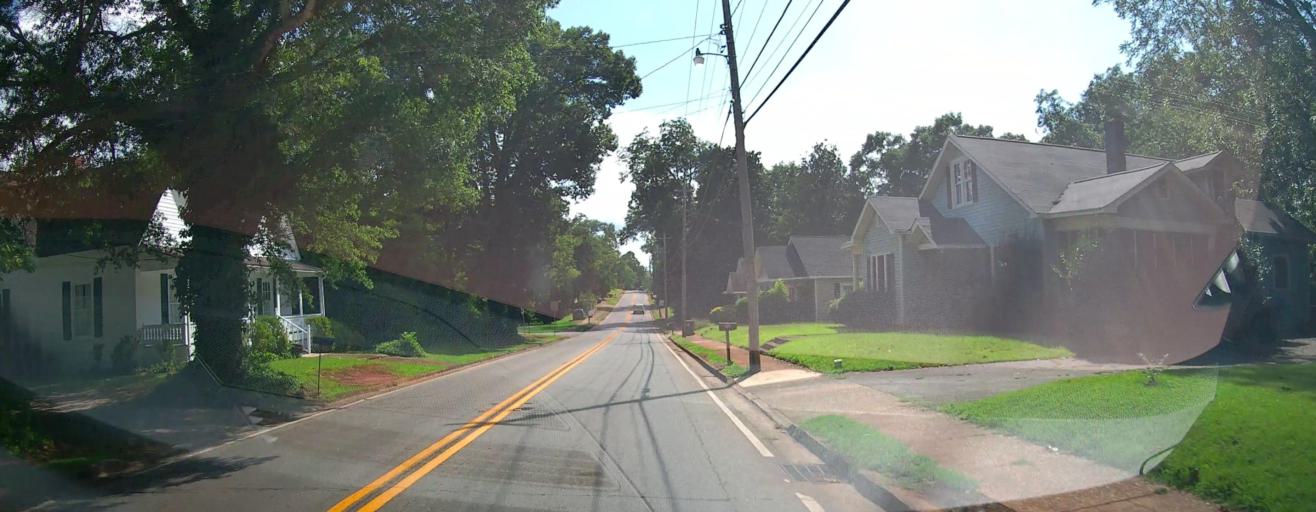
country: US
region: Georgia
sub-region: Upson County
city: Thomaston
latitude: 32.8839
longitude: -84.3290
